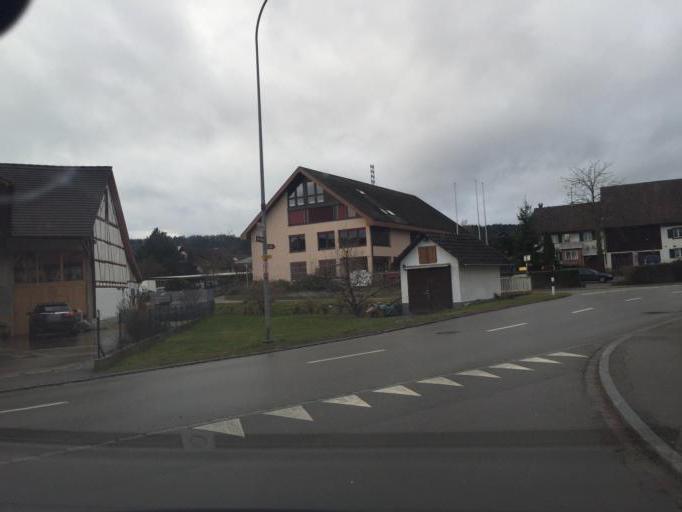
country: DE
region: Baden-Wuerttemberg
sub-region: Freiburg Region
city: Busingen
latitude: 47.6612
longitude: 8.7034
